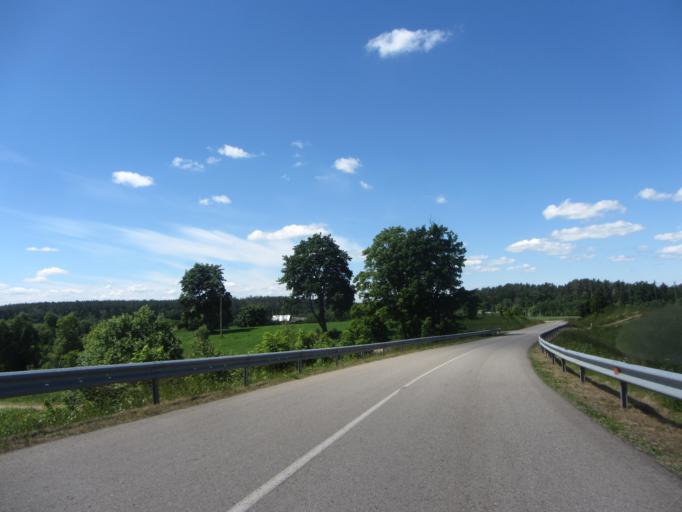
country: LT
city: Jieznas
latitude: 54.7474
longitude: 24.1838
